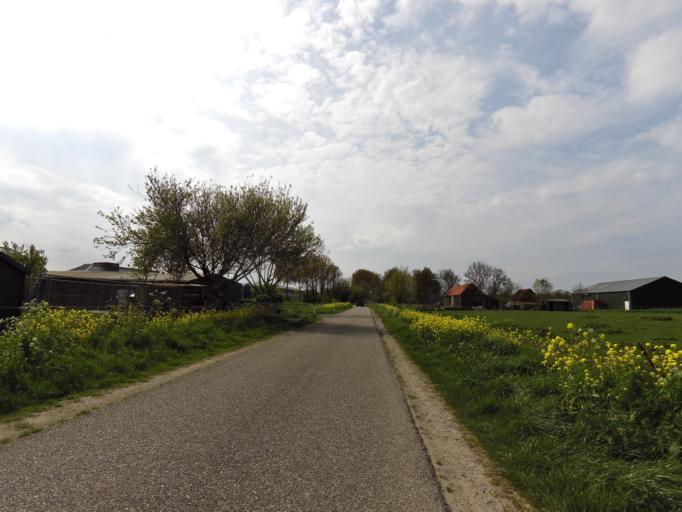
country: NL
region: South Holland
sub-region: Gemeente Brielle
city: Brielle
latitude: 51.8987
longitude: 4.1751
